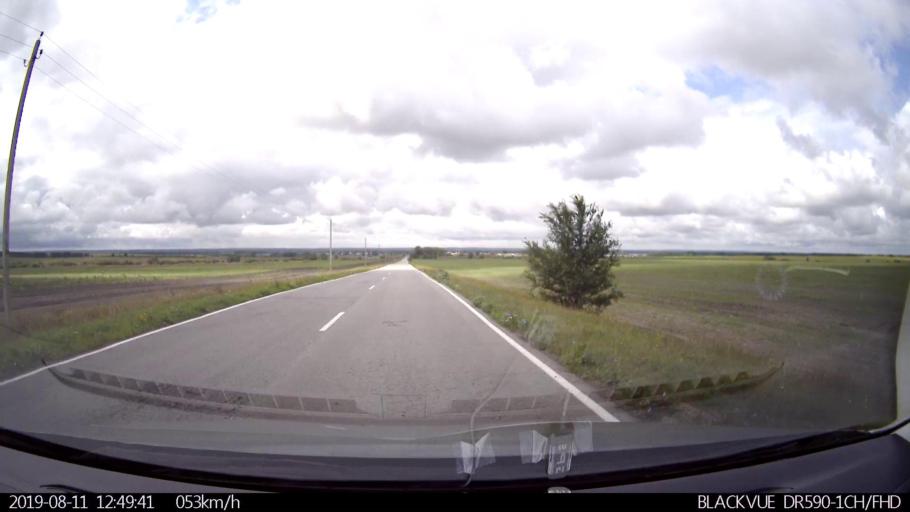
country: RU
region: Ulyanovsk
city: Ignatovka
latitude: 53.8754
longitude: 47.6831
